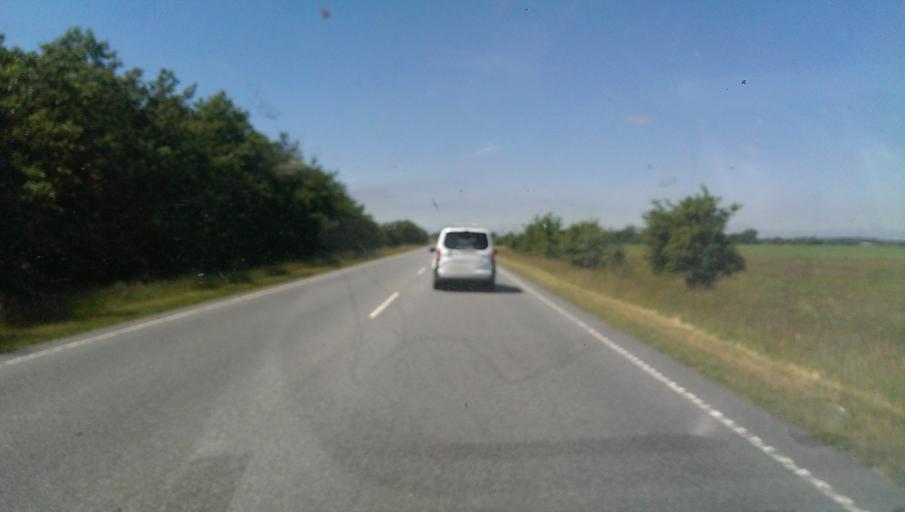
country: DK
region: South Denmark
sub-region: Esbjerg Kommune
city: Esbjerg
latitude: 55.5327
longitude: 8.4252
